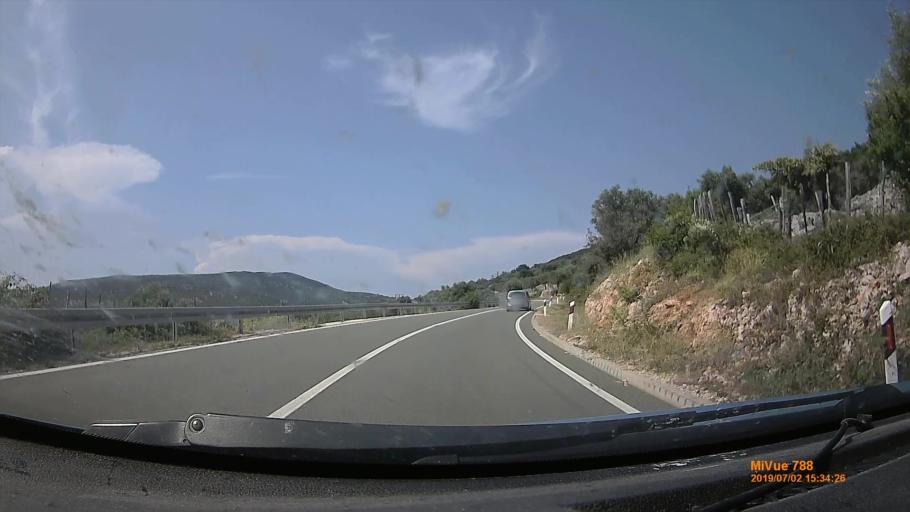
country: HR
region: Primorsko-Goranska
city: Cres
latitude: 44.9671
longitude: 14.4126
